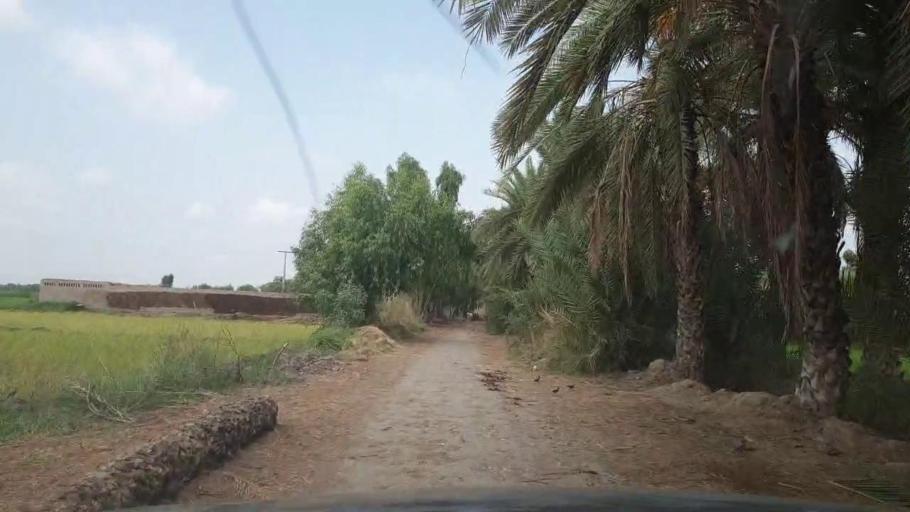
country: PK
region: Sindh
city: Ratodero
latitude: 27.8580
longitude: 68.2927
